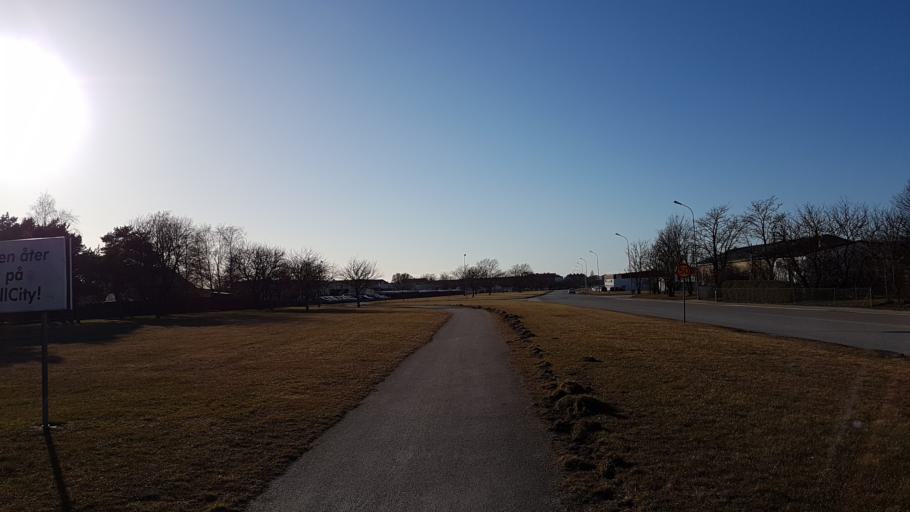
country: SE
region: Gotland
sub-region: Gotland
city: Visby
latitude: 57.6408
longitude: 18.3260
